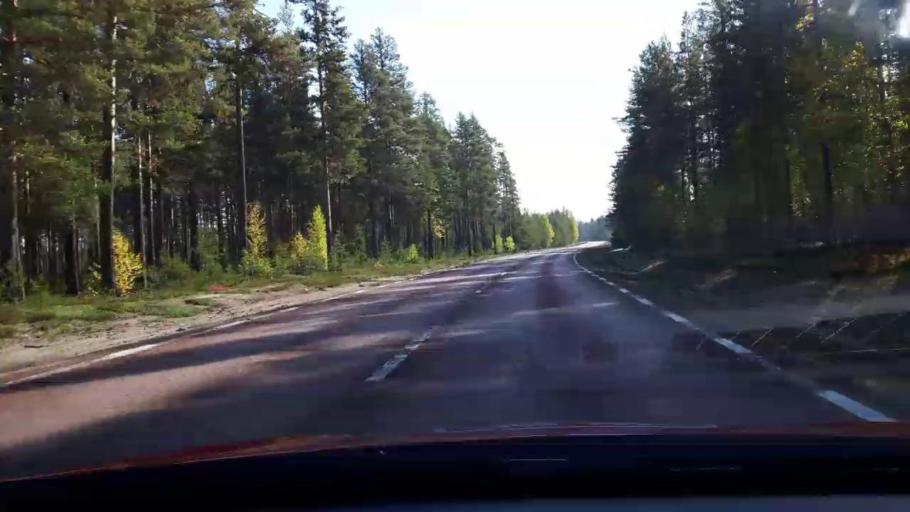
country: SE
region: Gaevleborg
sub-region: Ljusdals Kommun
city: Farila
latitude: 61.9228
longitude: 15.6023
